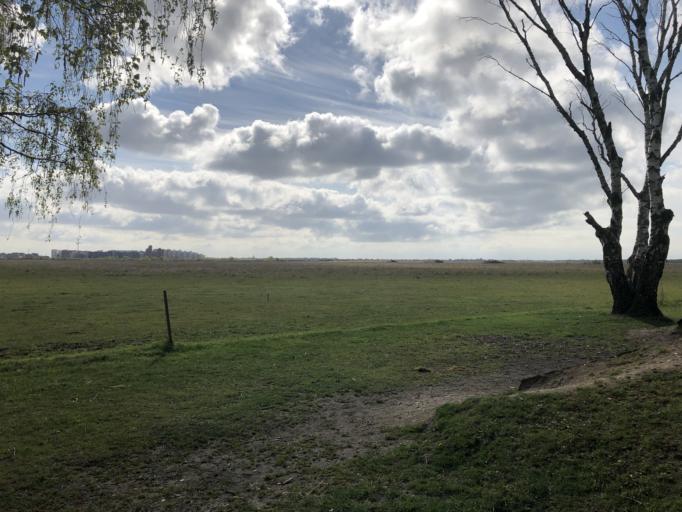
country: DK
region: Capital Region
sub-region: Frederiksberg Kommune
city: Frederiksberg
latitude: 55.6218
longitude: 12.5384
